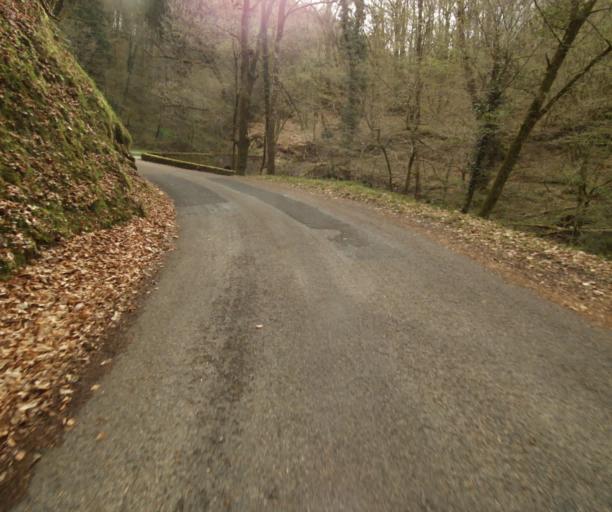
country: FR
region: Limousin
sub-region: Departement de la Correze
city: Argentat
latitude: 45.1987
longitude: 1.9705
